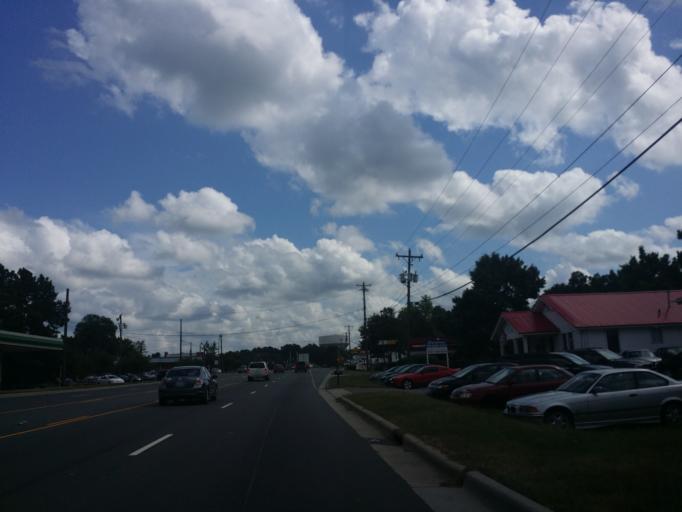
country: US
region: North Carolina
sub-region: Durham County
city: Durham
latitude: 35.9520
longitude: -78.8390
